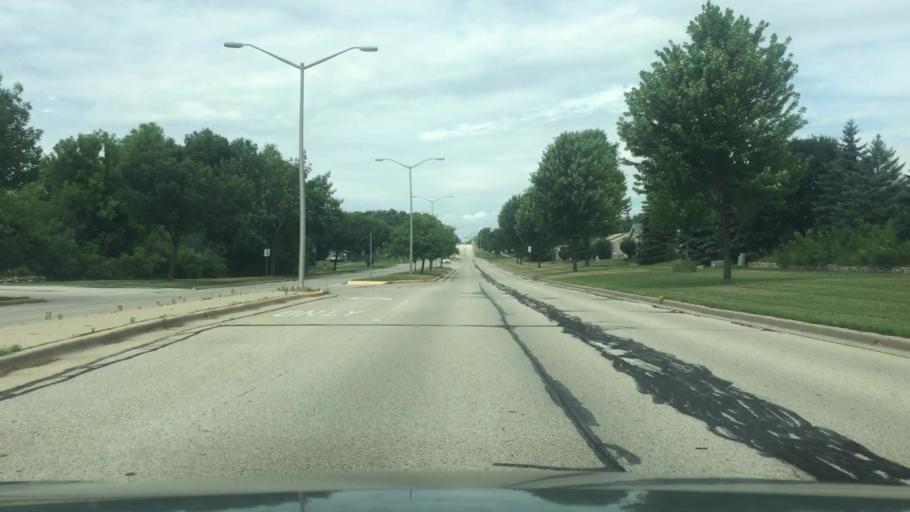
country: US
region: Wisconsin
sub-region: Waukesha County
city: Waukesha
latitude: 42.9792
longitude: -88.2274
